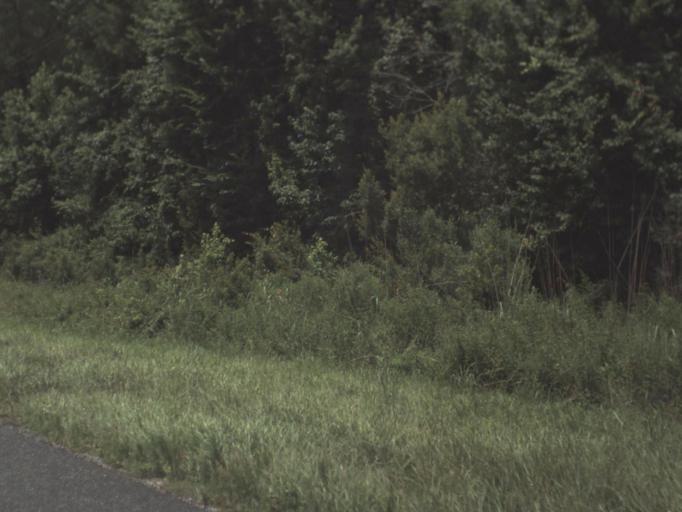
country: US
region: Florida
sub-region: Taylor County
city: Perry
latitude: 30.2910
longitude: -83.7369
